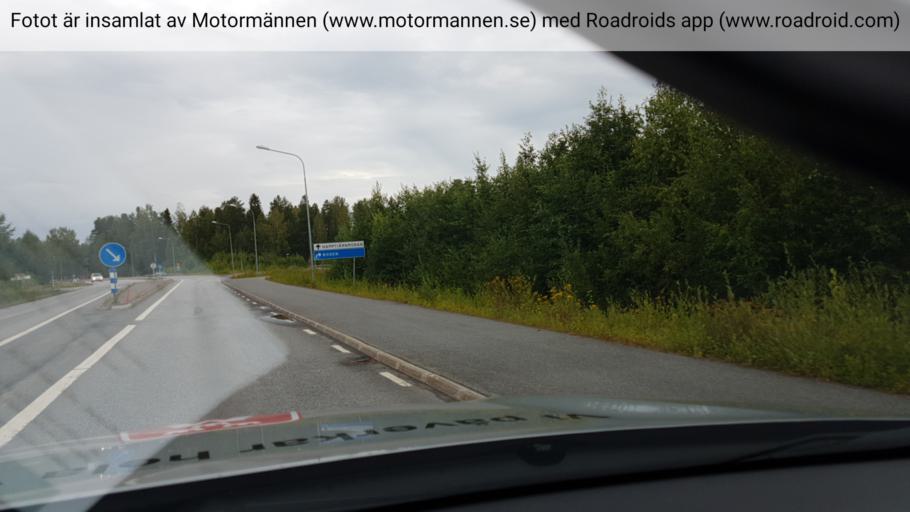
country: SE
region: Norrbotten
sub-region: Bodens Kommun
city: Boden
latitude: 65.8135
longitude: 21.6493
